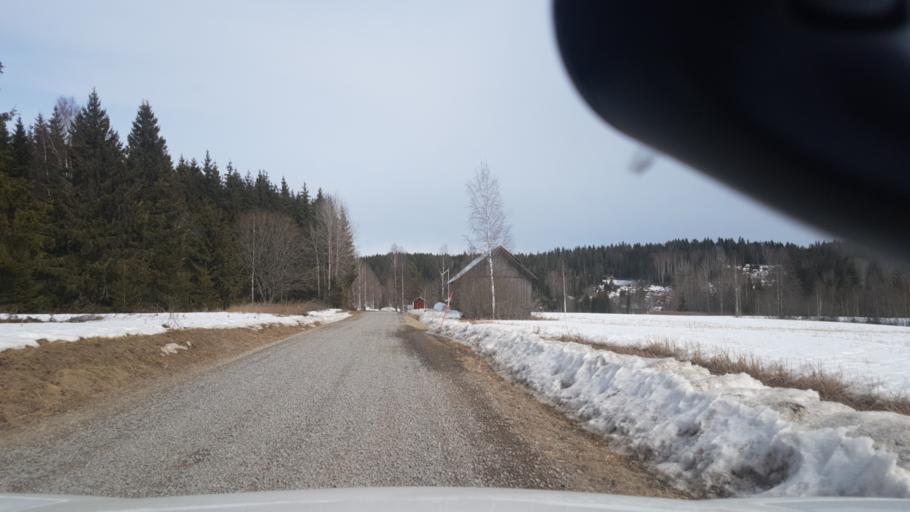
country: SE
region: Vaermland
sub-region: Eda Kommun
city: Charlottenberg
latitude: 59.8384
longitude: 12.3561
